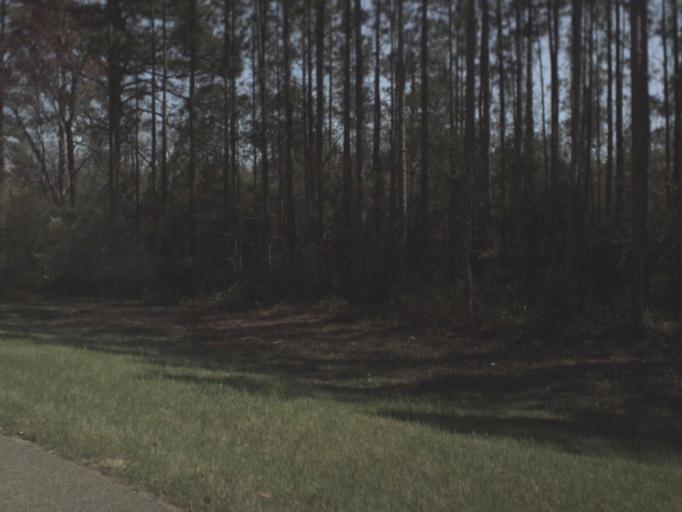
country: US
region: Florida
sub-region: Liberty County
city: Bristol
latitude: 30.4181
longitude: -84.8824
